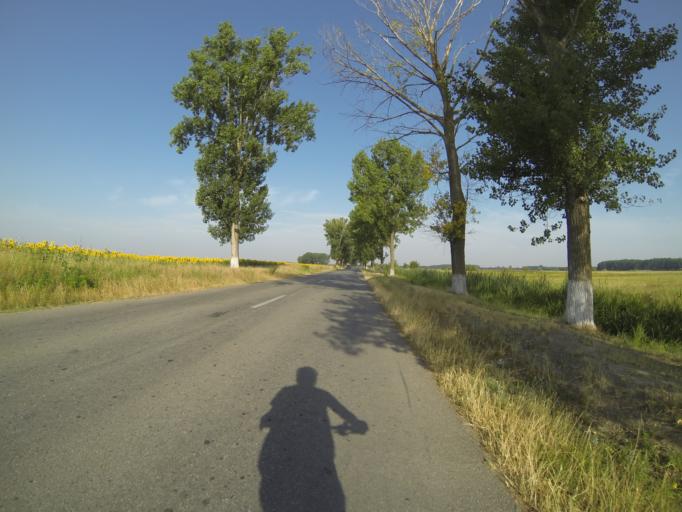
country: RO
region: Dolj
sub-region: Comuna Dobresti
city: Dobresti
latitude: 43.9829
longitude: 23.9270
